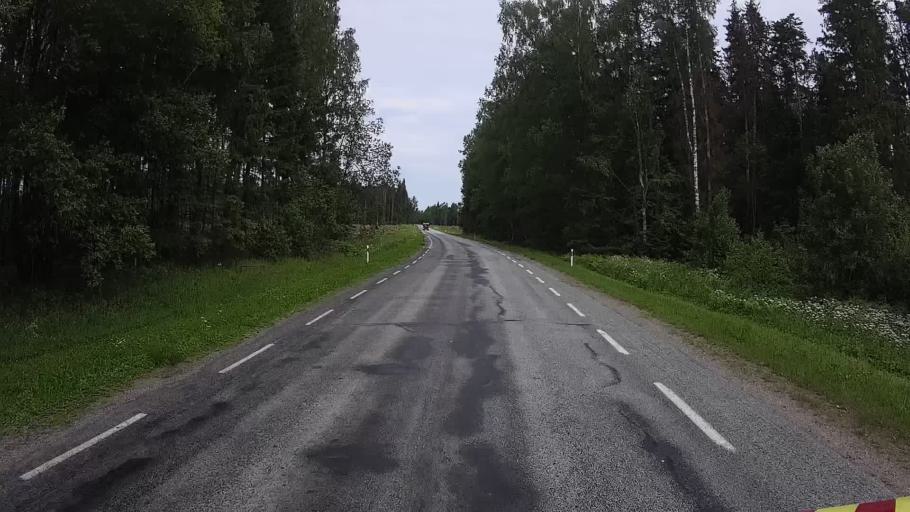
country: EE
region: Viljandimaa
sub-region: Karksi vald
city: Karksi-Nuia
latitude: 58.2181
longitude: 25.6188
